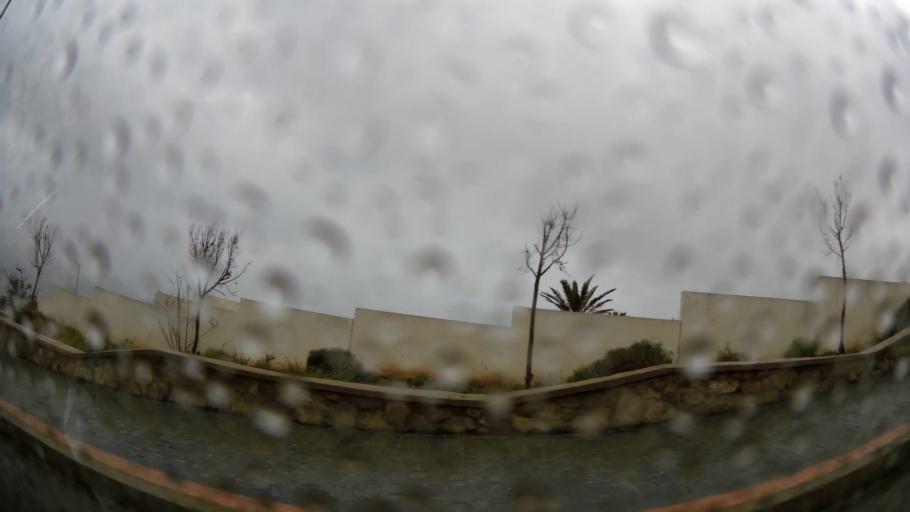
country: MA
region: Taza-Al Hoceima-Taounate
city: Al Hoceima
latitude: 35.2517
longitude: -3.9470
